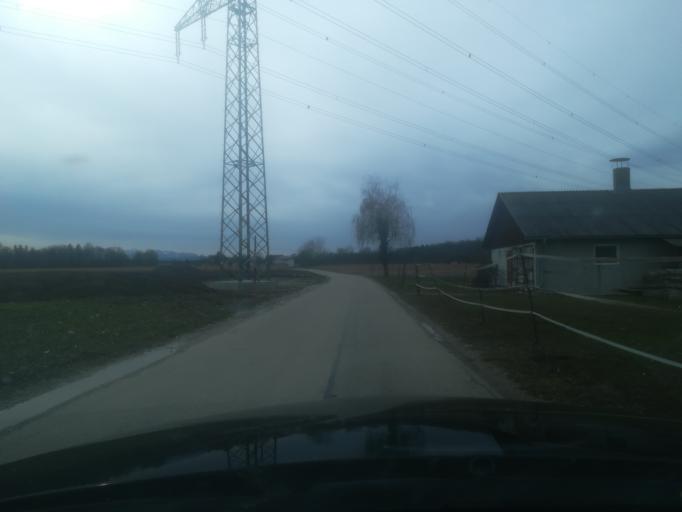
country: AT
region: Upper Austria
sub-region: Wels-Land
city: Gunskirchen
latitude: 48.1026
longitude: 13.9274
